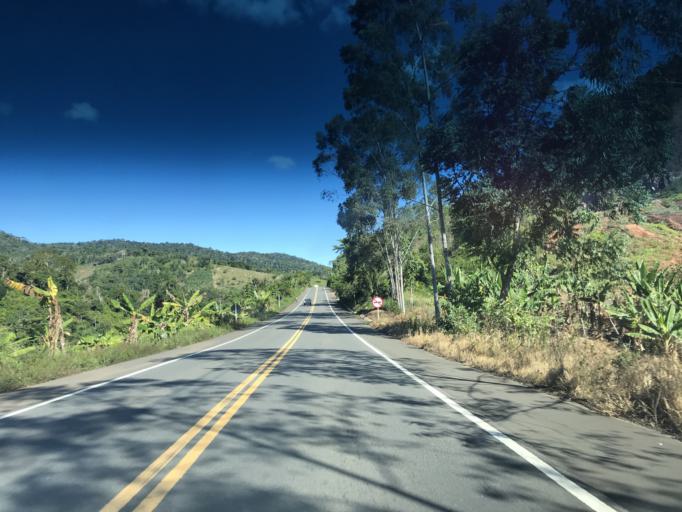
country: BR
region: Bahia
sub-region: Gandu
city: Gandu
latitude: -13.8908
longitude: -39.4788
